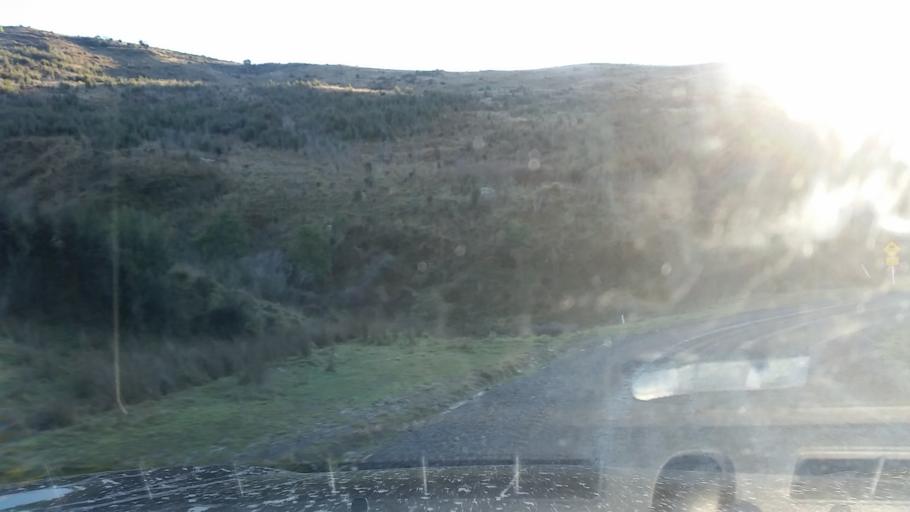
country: NZ
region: Marlborough
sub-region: Marlborough District
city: Blenheim
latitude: -41.7850
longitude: 173.8062
